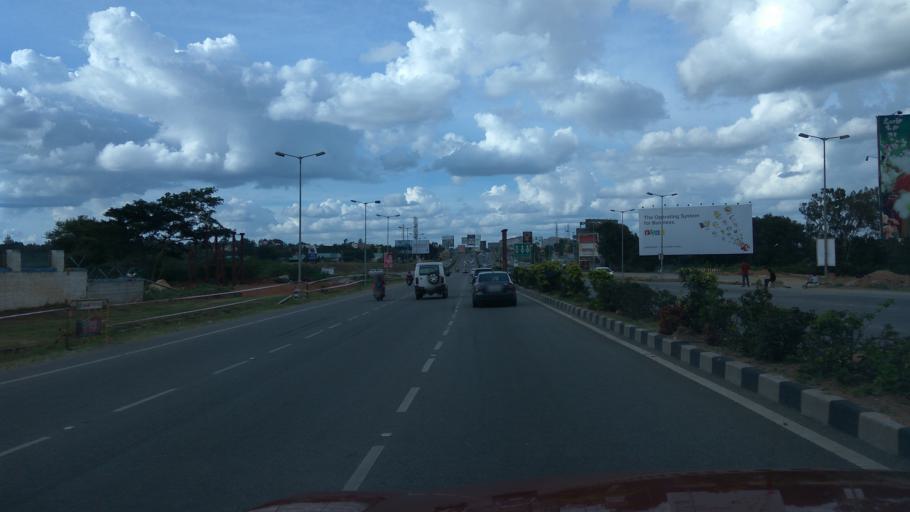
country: IN
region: Karnataka
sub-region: Bangalore Urban
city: Yelahanka
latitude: 13.1370
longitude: 77.6175
